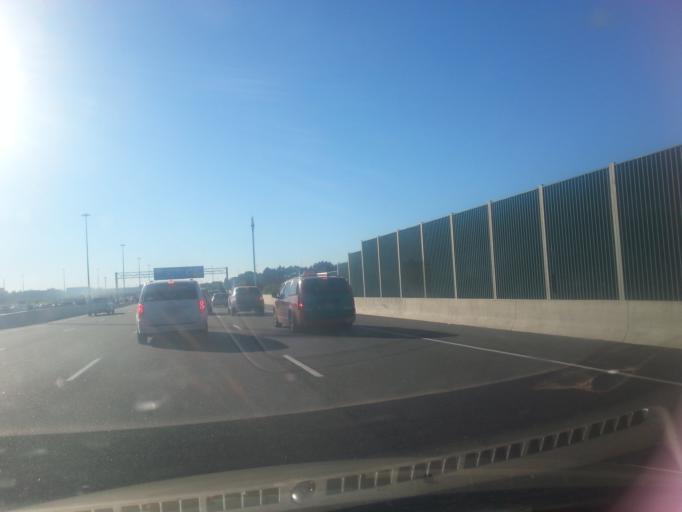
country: CA
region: Ontario
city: Concord
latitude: 43.7181
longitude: -79.5069
